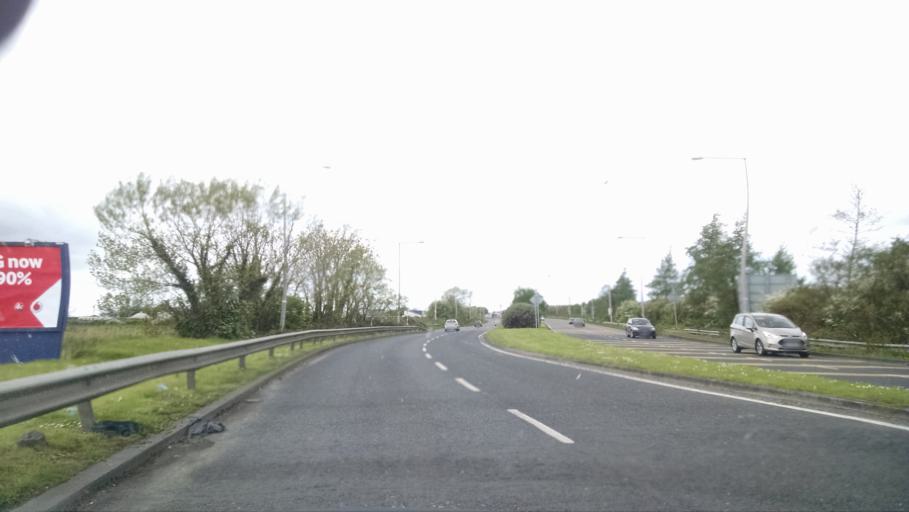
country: IE
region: Munster
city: Moyross
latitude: 52.6765
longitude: -8.6827
